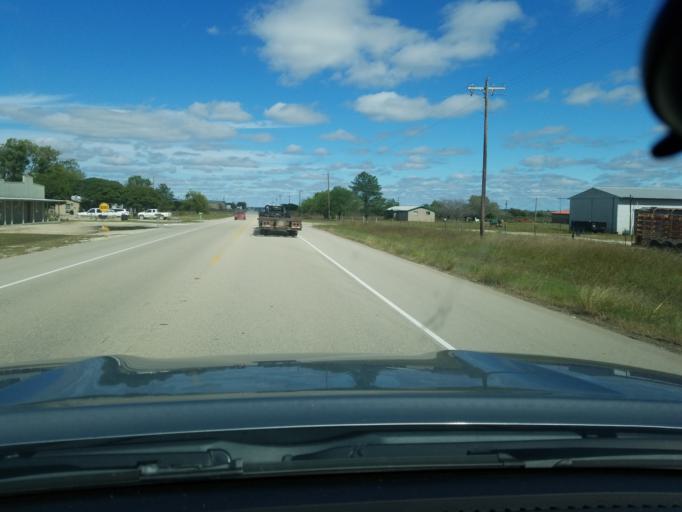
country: US
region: Texas
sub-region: Hamilton County
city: Hamilton
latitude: 31.6654
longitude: -98.1400
